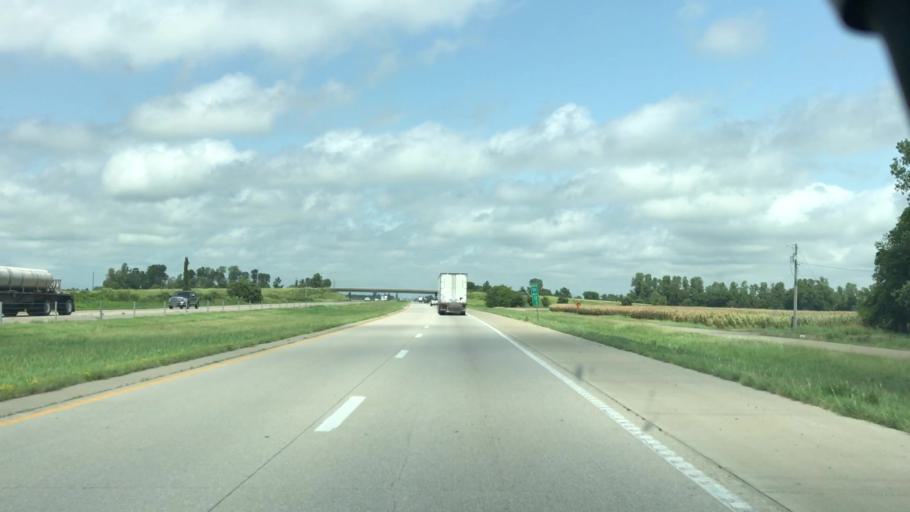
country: US
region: Missouri
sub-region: Pemiscot County
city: Steele
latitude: 36.1349
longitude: -89.7530
